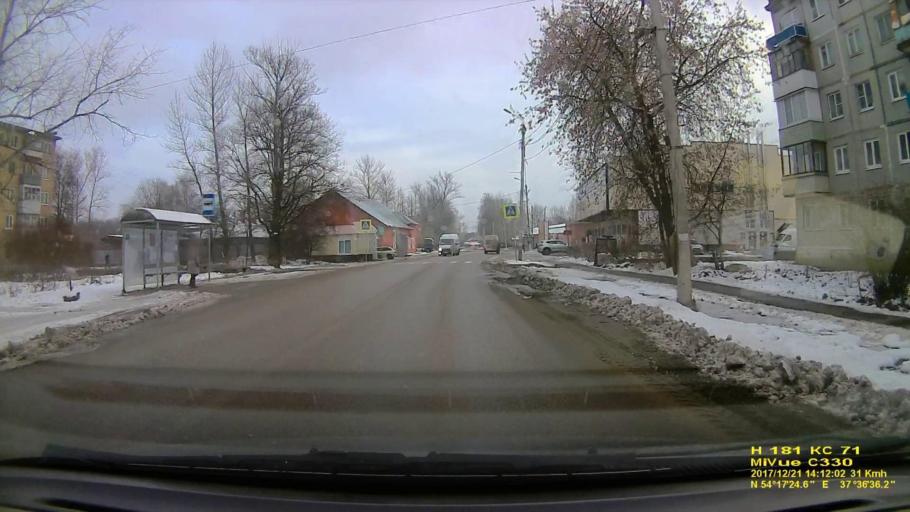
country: RU
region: Tula
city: Gorelki
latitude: 54.2902
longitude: 37.6101
